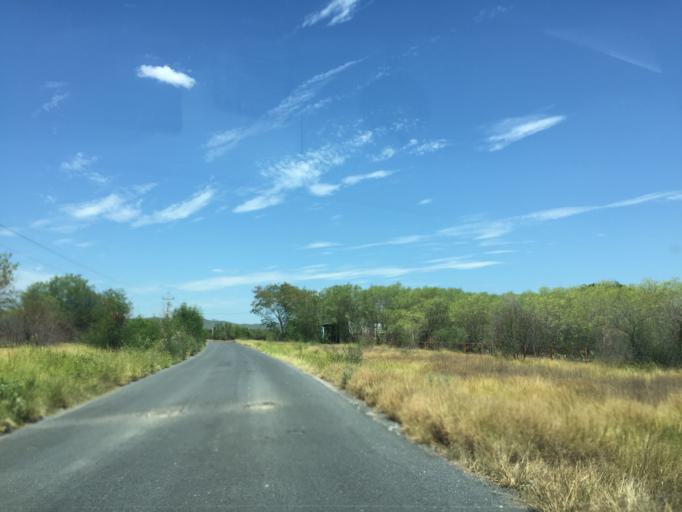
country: MX
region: Nuevo Leon
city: Marin
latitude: 25.8306
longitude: -99.9058
